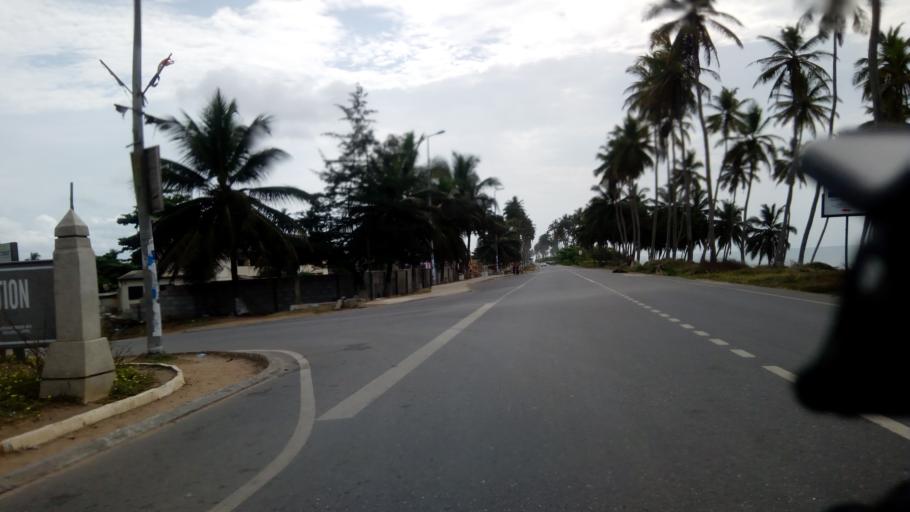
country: GH
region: Central
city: Cape Coast
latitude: 5.1013
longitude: -1.2719
